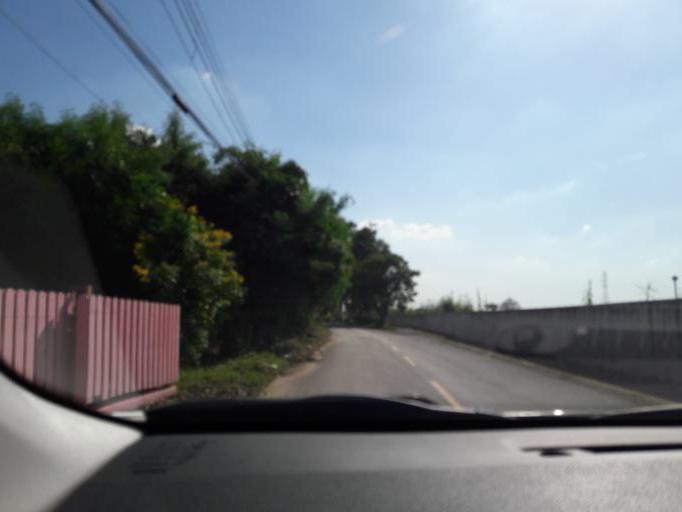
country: TH
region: Ang Thong
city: Ang Thong
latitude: 14.5844
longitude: 100.4489
